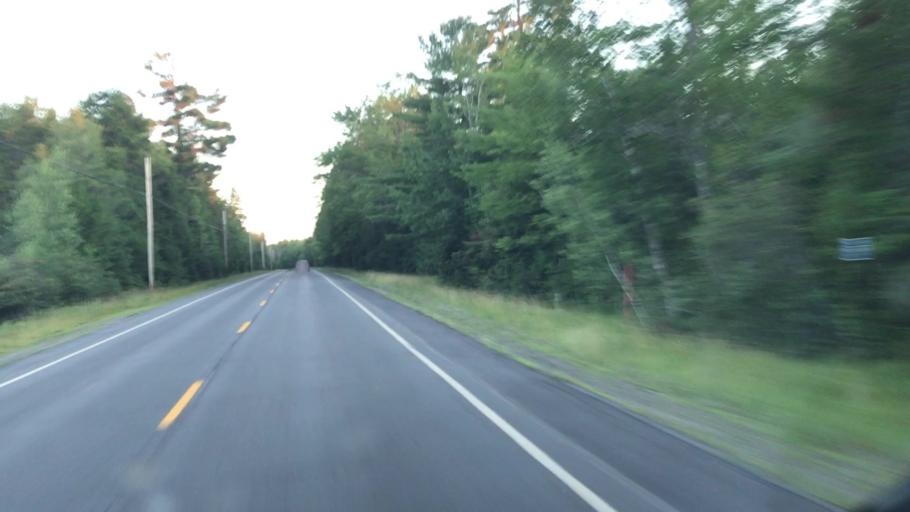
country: US
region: Maine
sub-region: Penobscot County
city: Medway
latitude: 45.5807
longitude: -68.3178
